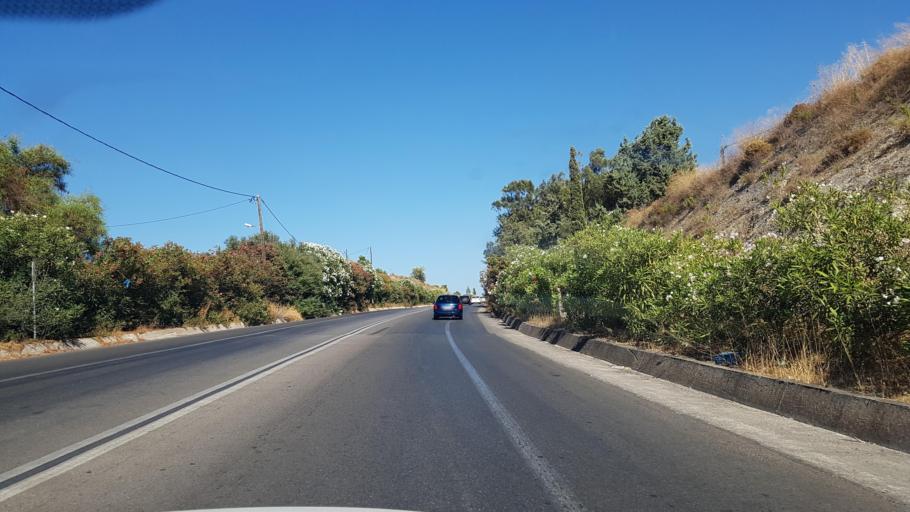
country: GR
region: Crete
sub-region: Nomos Chanias
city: Galatas
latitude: 35.5064
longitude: 23.9685
